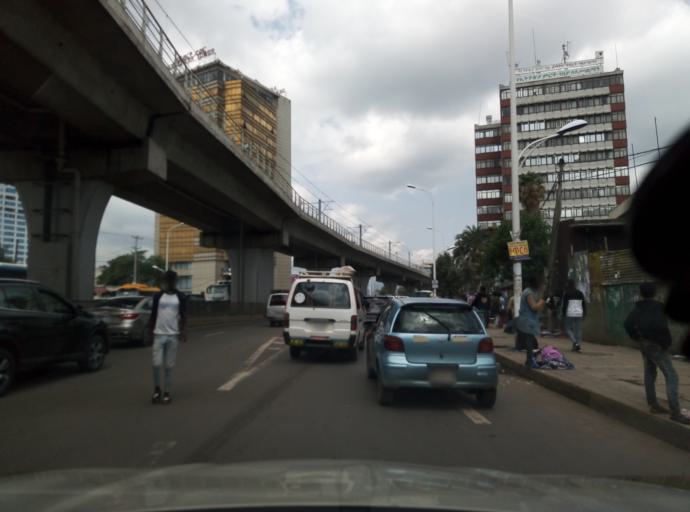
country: ET
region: Adis Abeba
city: Addis Ababa
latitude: 9.0109
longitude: 38.7483
